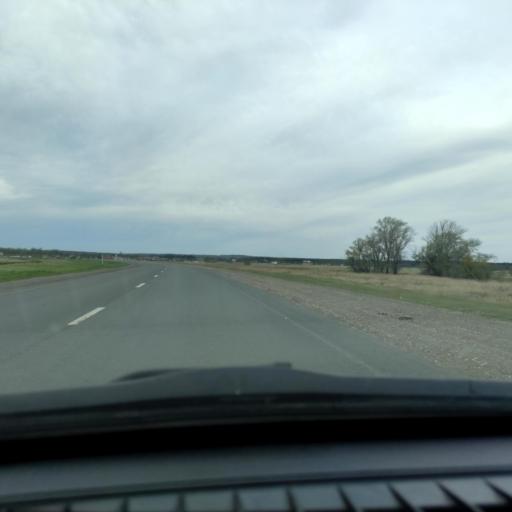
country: RU
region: Samara
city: Krasnyy Yar
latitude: 53.5340
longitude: 50.3577
